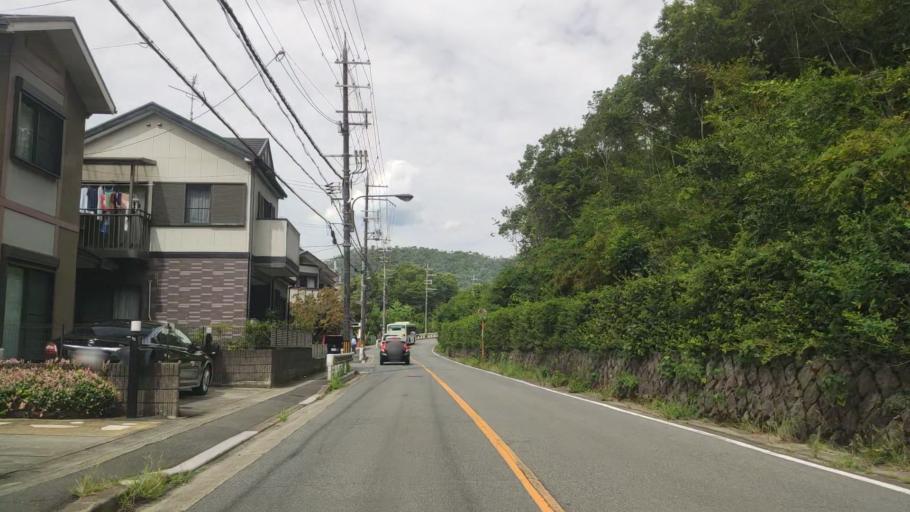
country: JP
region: Kyoto
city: Kyoto
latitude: 35.0253
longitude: 135.6966
